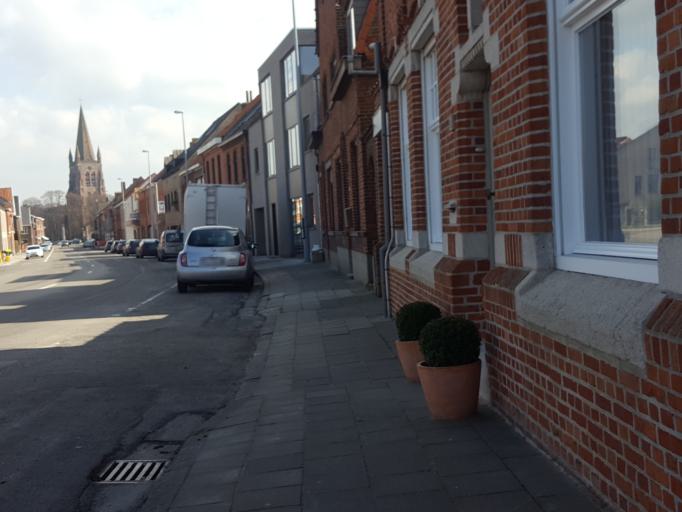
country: BE
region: Flanders
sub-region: Provincie West-Vlaanderen
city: Ieper
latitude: 50.9140
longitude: 2.9133
